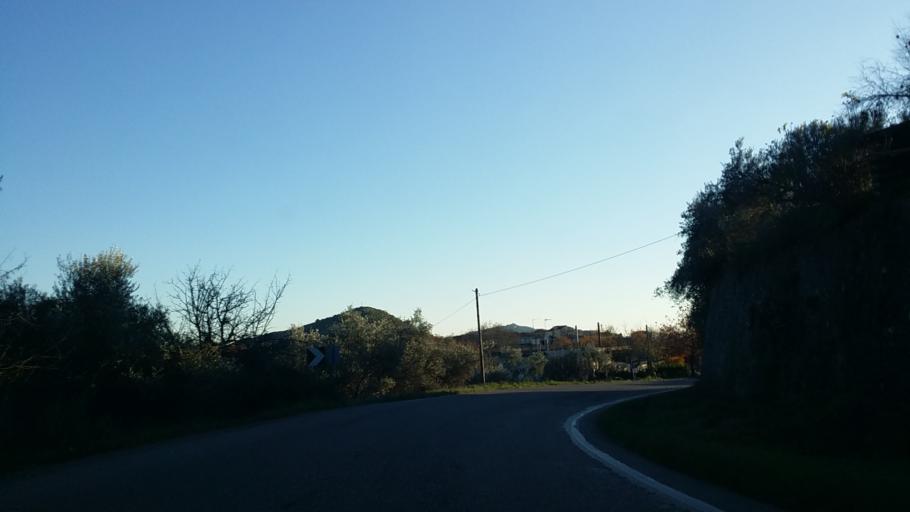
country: GR
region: West Greece
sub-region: Nomos Aitolias kai Akarnanias
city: Lepenou
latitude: 38.7419
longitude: 21.3464
